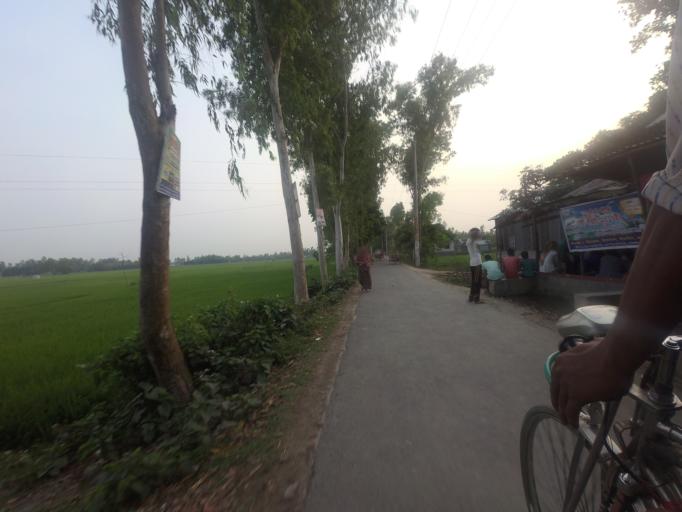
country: BD
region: Rajshahi
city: Sirajganj
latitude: 24.3278
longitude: 89.6776
